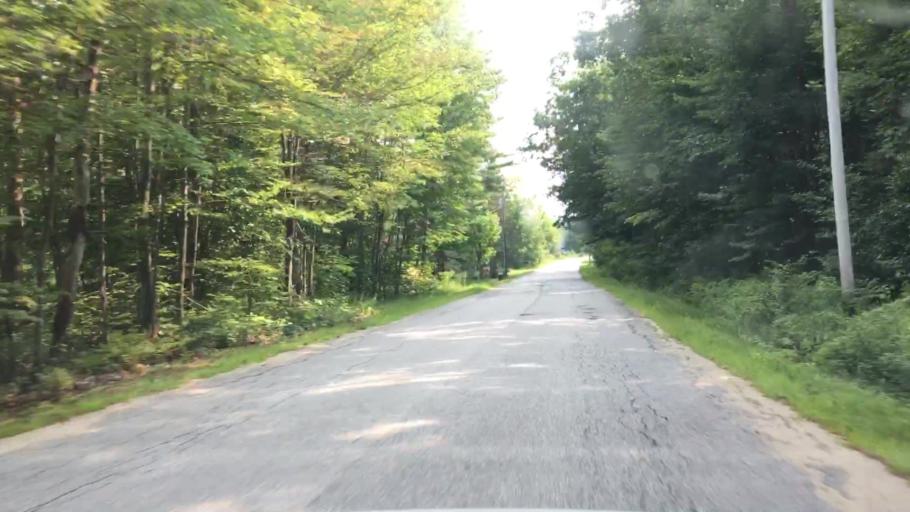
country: US
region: Maine
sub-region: Androscoggin County
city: Livermore
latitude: 44.3292
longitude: -70.2899
